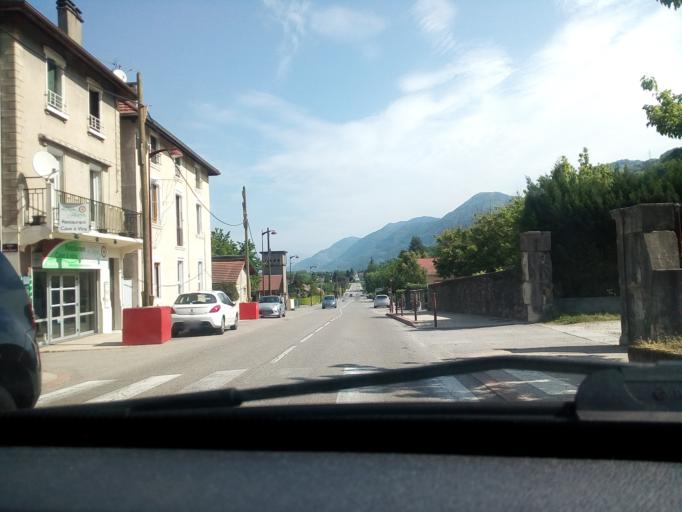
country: FR
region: Rhone-Alpes
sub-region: Departement de l'Isere
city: Froges
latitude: 45.2748
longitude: 5.9261
